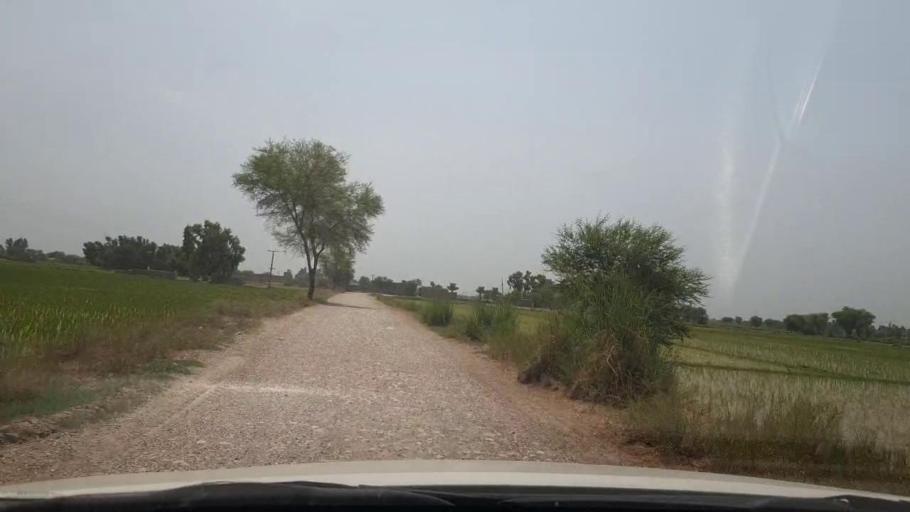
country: PK
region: Sindh
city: Rustam jo Goth
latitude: 28.0080
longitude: 68.7681
